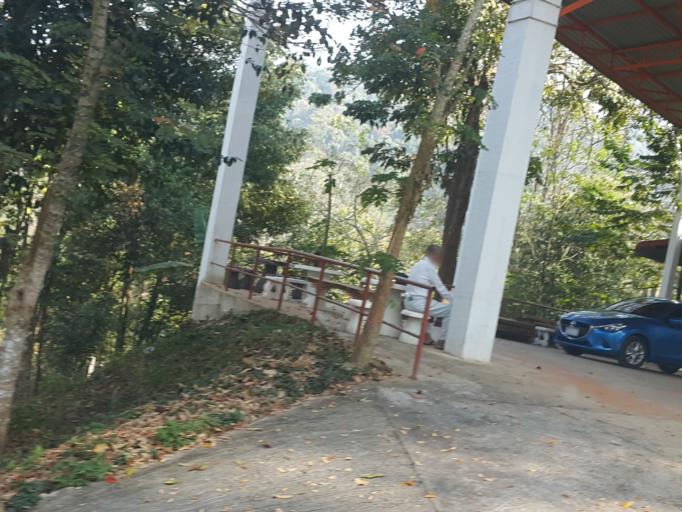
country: TH
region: Chiang Mai
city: Samoeng
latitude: 19.0165
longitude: 98.7585
